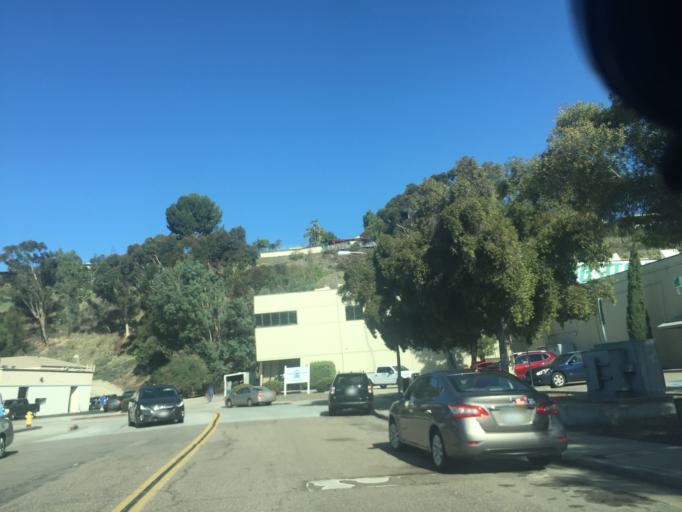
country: US
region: California
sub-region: San Diego County
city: La Mesa
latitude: 32.7821
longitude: -117.0920
